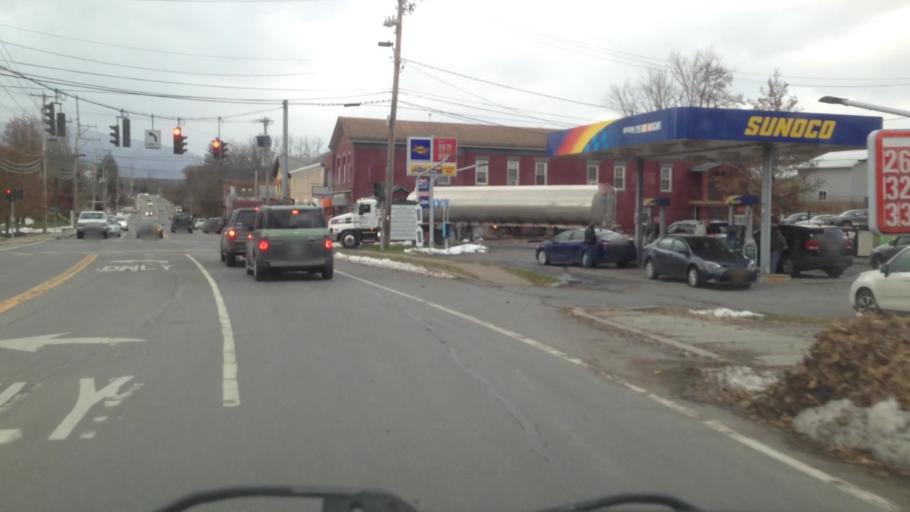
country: US
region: New York
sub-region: Ulster County
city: Saugerties
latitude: 42.0805
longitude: -73.9595
